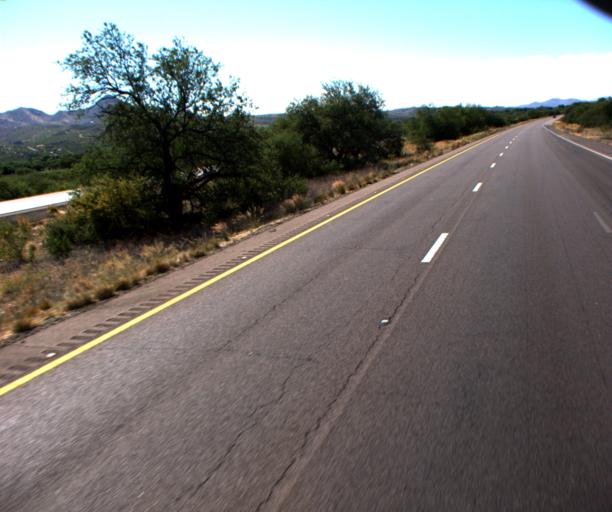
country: US
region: Arizona
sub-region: Santa Cruz County
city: Rio Rico
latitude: 31.5244
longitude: -111.0213
